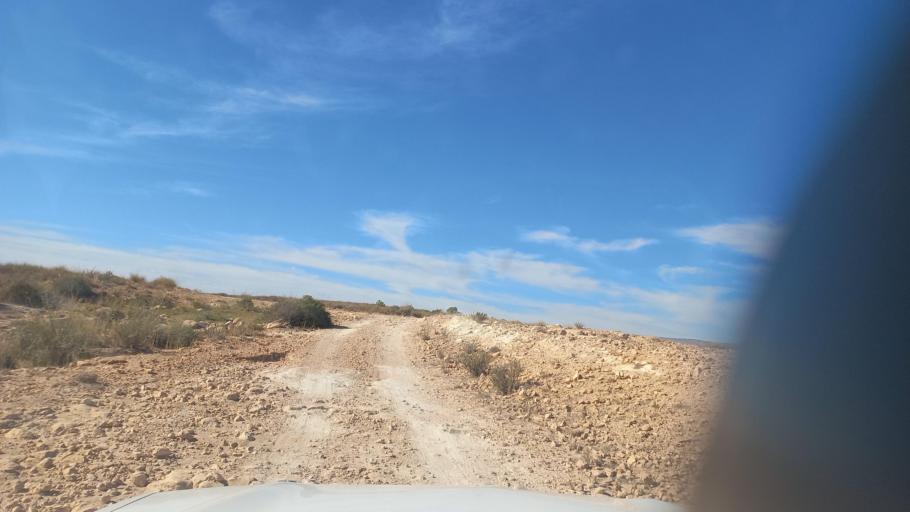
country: TN
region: Al Qasrayn
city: Kasserine
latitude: 35.2147
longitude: 8.9806
